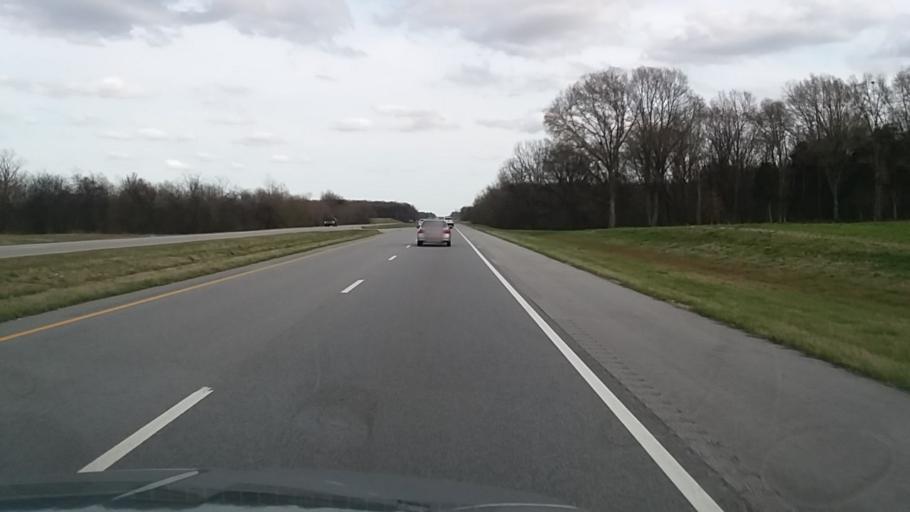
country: US
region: Alabama
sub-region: Lawrence County
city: Town Creek
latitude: 34.6831
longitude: -87.4951
